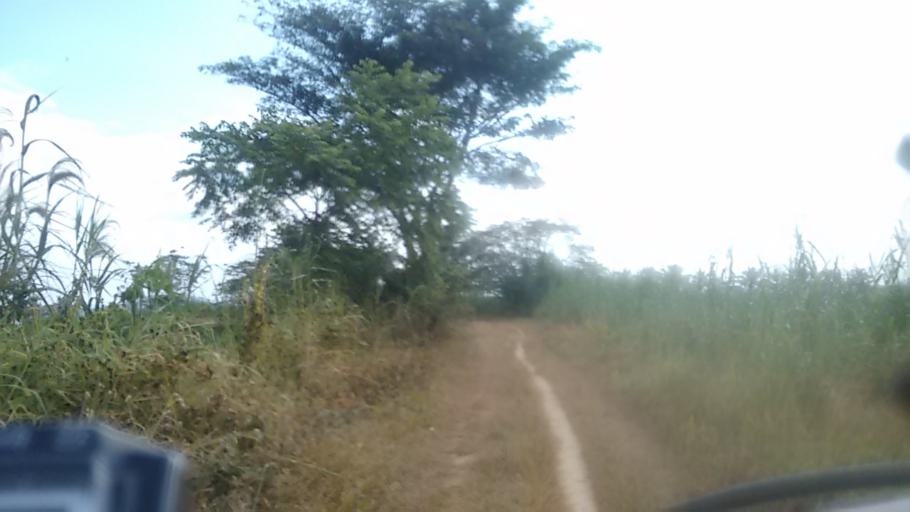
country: IN
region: Kerala
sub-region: Thrissur District
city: Trichur
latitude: 10.5298
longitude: 76.1450
